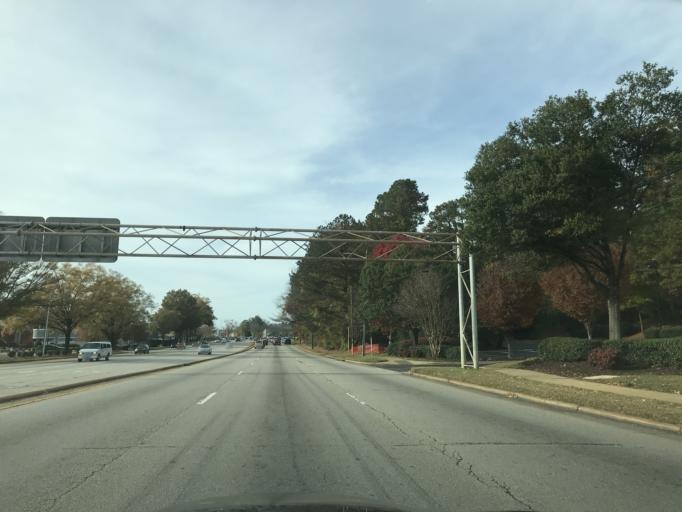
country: US
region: North Carolina
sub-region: Wake County
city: West Raleigh
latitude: 35.8382
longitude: -78.6737
